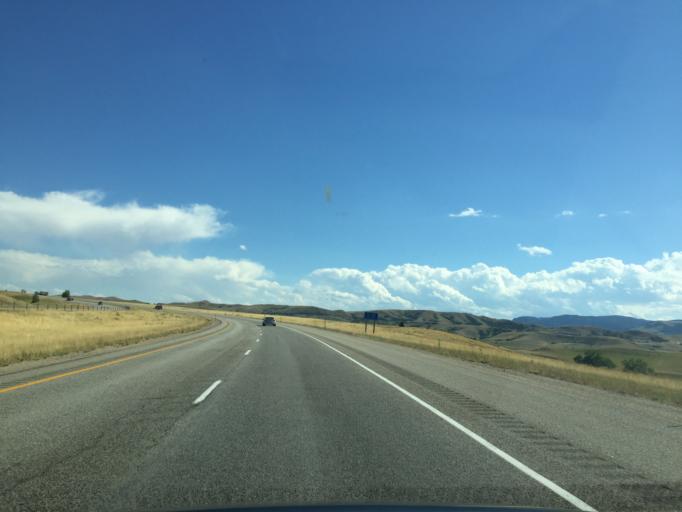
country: US
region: Wyoming
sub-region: Sheridan County
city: Sheridan
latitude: 44.6061
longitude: -106.8482
